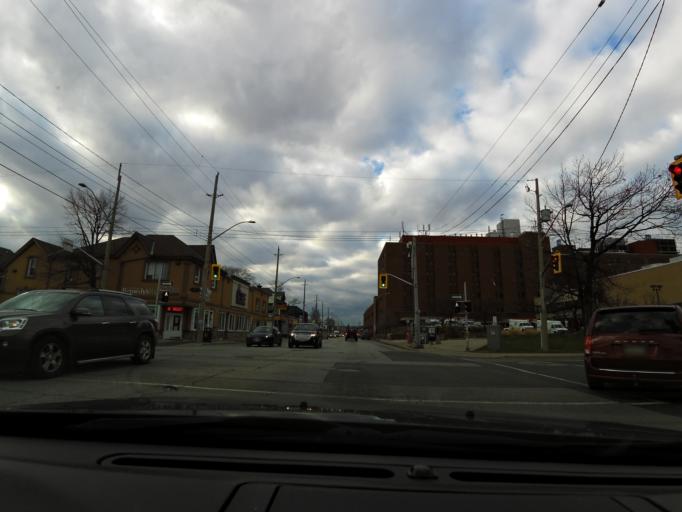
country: CA
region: Ontario
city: Hamilton
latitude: 43.2610
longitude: -79.8531
